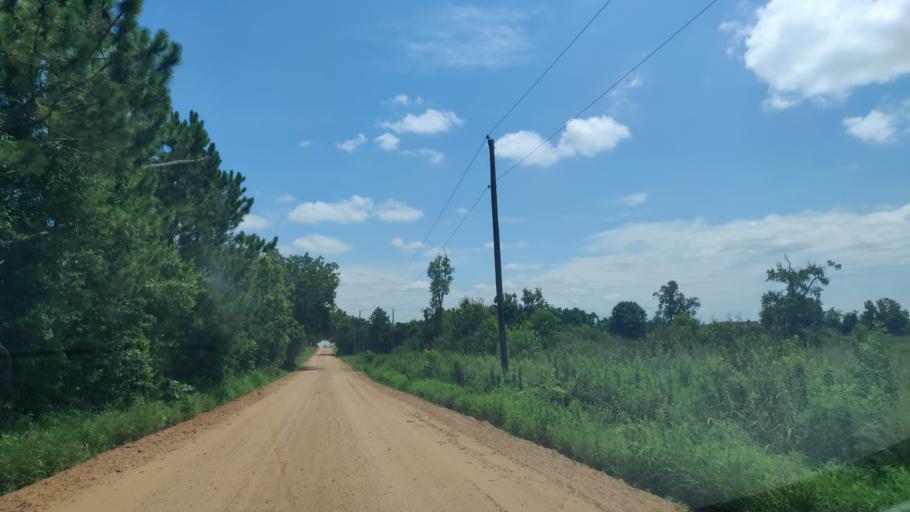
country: US
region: Georgia
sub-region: Tift County
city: Tifton
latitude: 31.4644
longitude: -83.6374
